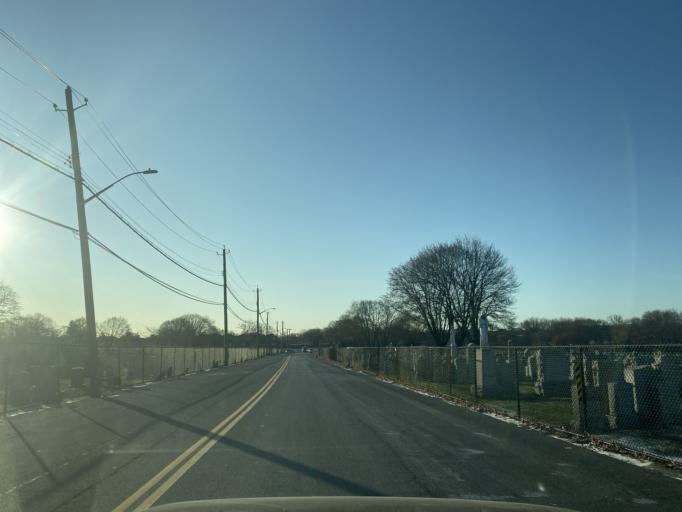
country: US
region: New York
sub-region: Bronx
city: The Bronx
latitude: 40.8336
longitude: -73.8352
